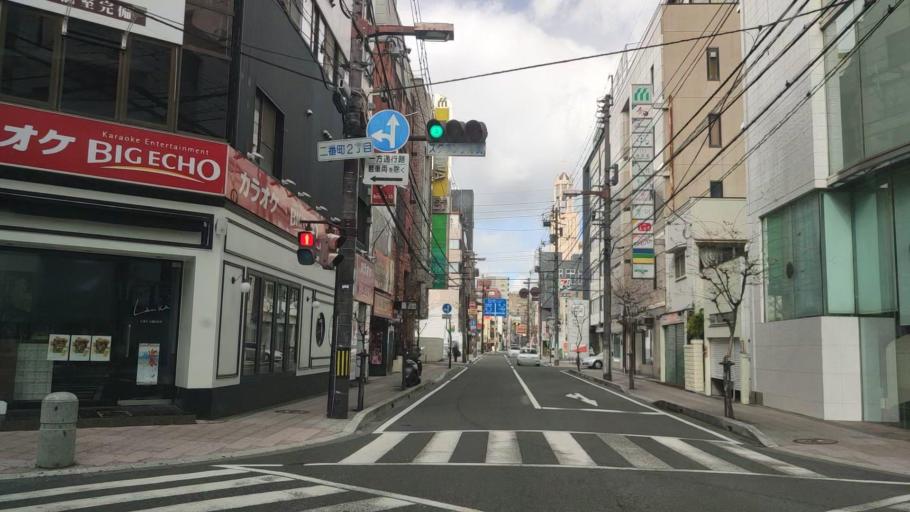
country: JP
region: Ehime
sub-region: Shikoku-chuo Shi
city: Matsuyama
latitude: 33.8400
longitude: 132.7722
